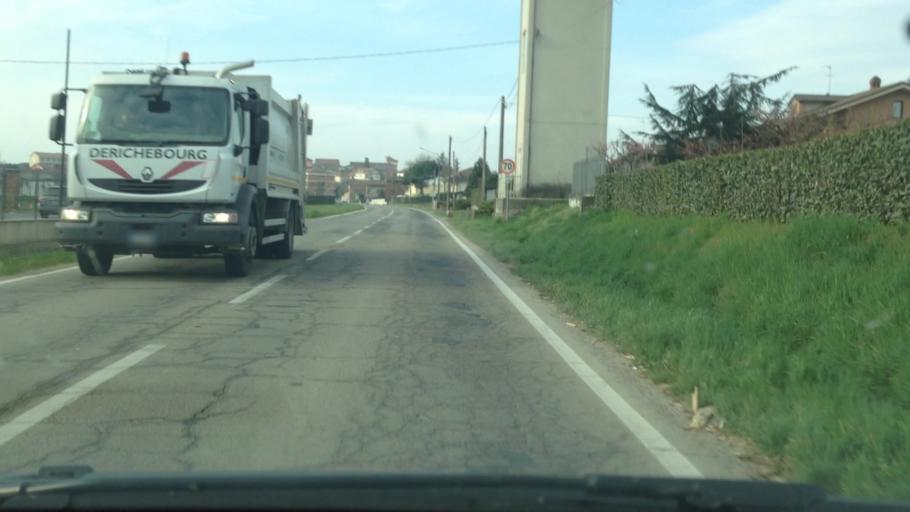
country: IT
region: Piedmont
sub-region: Provincia di Asti
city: San Damiano d'Asti
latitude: 44.8424
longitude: 8.0687
